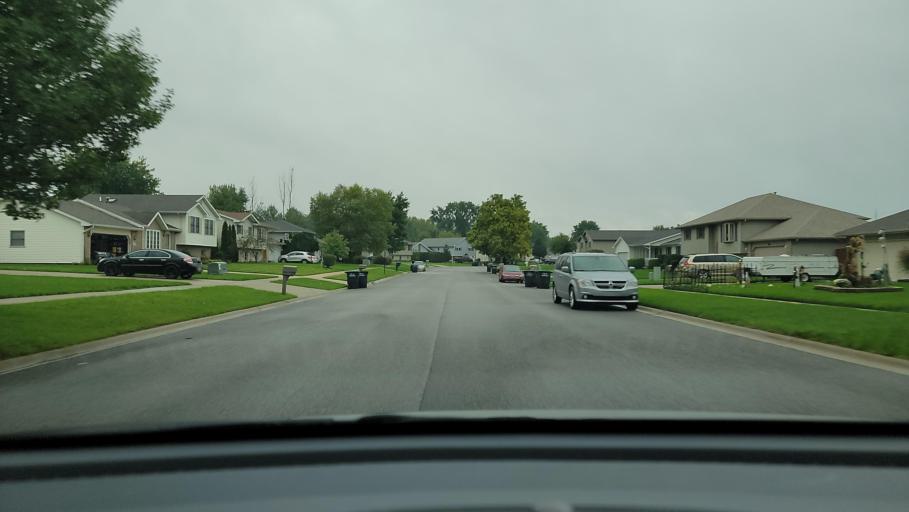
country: US
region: Indiana
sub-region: Porter County
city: Portage
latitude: 41.5634
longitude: -87.1761
